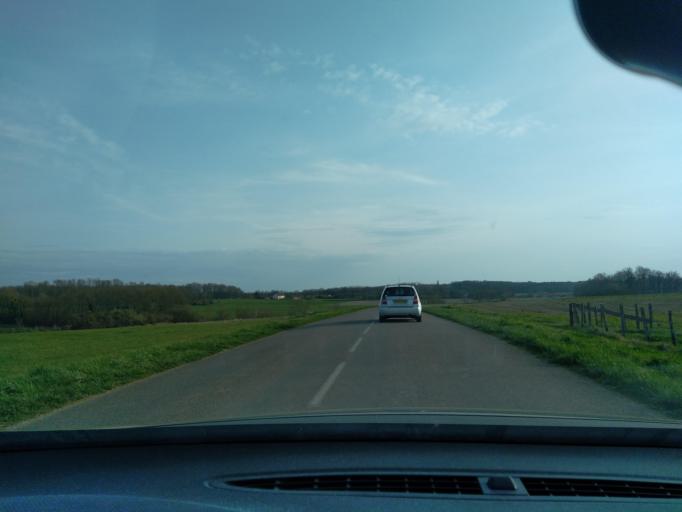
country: FR
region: Franche-Comte
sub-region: Departement du Jura
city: Chaussin
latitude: 46.9718
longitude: 5.4244
